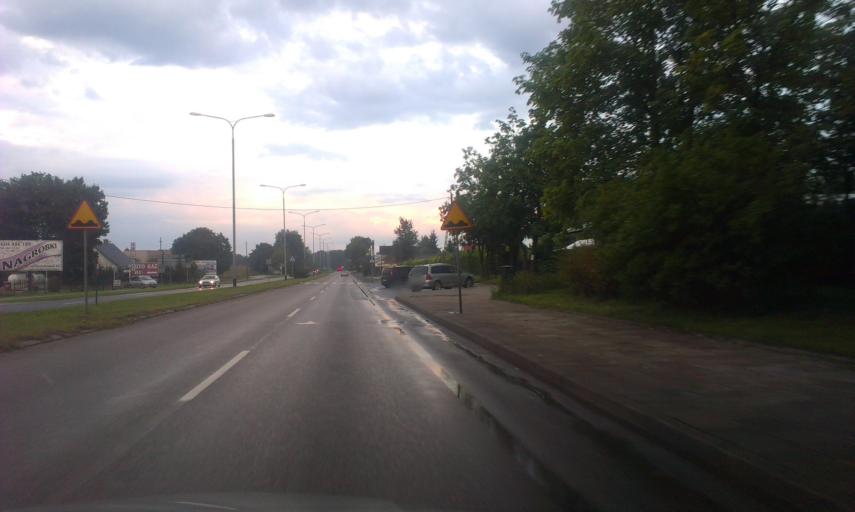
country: PL
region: West Pomeranian Voivodeship
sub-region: Koszalin
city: Koszalin
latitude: 54.1721
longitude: 16.2039
